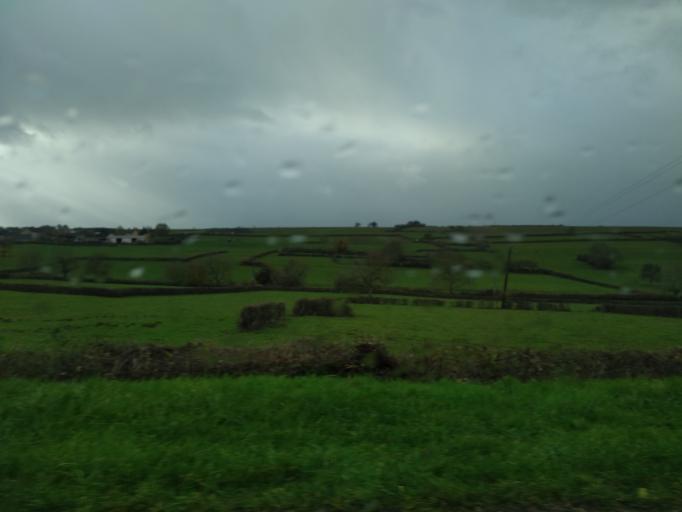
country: FR
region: Bourgogne
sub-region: Departement de Saone-et-Loire
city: Saint-Leger-sur-Dheune
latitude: 46.8499
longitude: 4.6857
